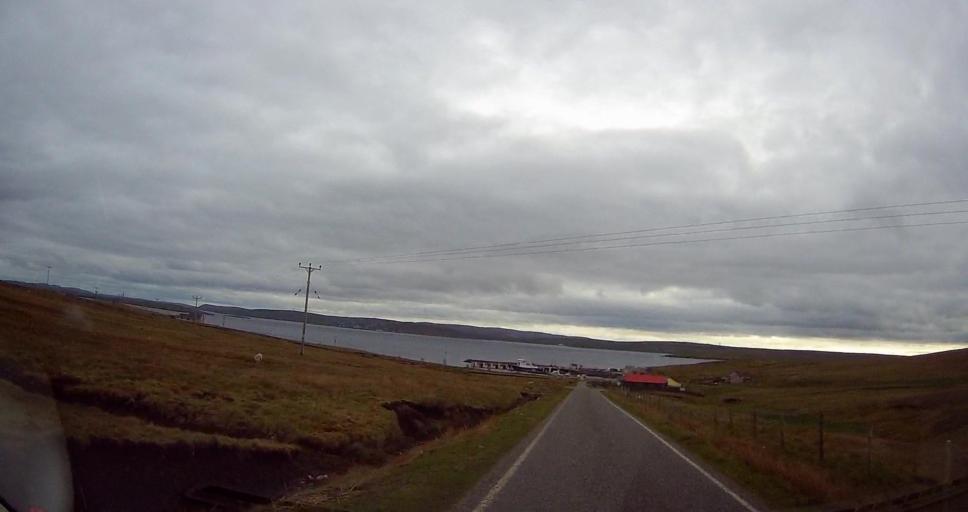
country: GB
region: Scotland
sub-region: Shetland Islands
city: Shetland
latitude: 60.5005
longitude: -1.1521
